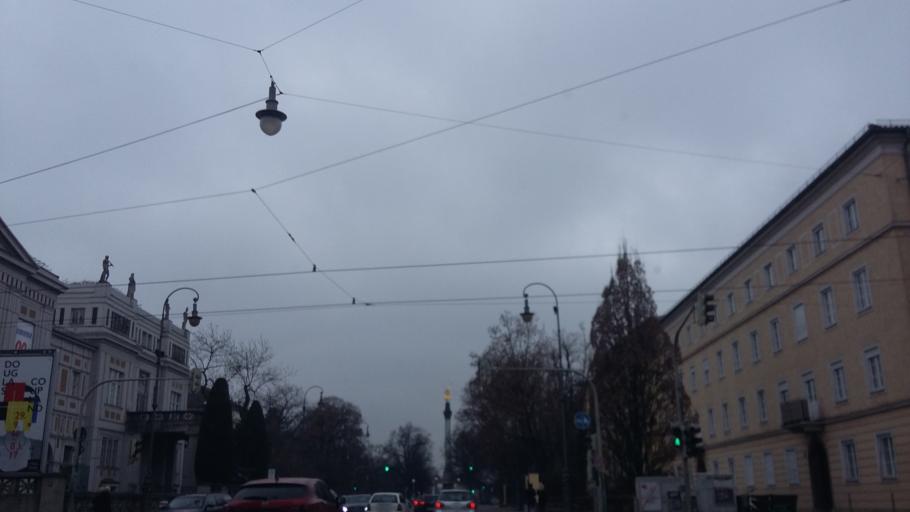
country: DE
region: Bavaria
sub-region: Upper Bavaria
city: Bogenhausen
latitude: 48.1407
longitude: 11.6004
